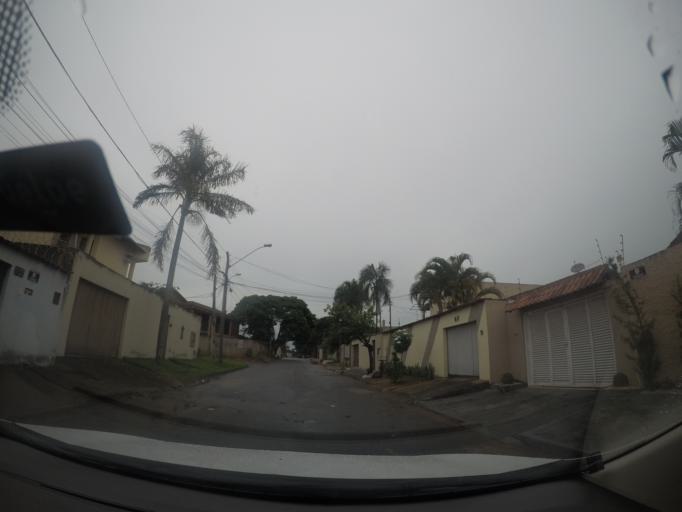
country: BR
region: Goias
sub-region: Goiania
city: Goiania
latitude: -16.6347
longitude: -49.2314
